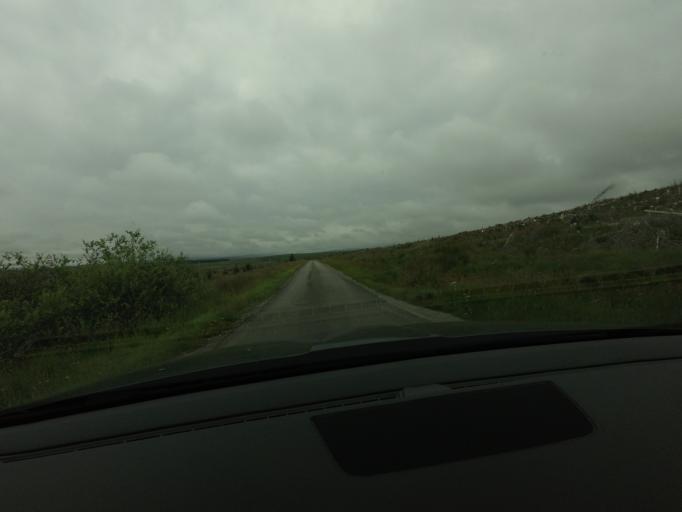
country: GB
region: Scotland
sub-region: Highland
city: Evanton
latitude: 58.1567
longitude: -4.4894
